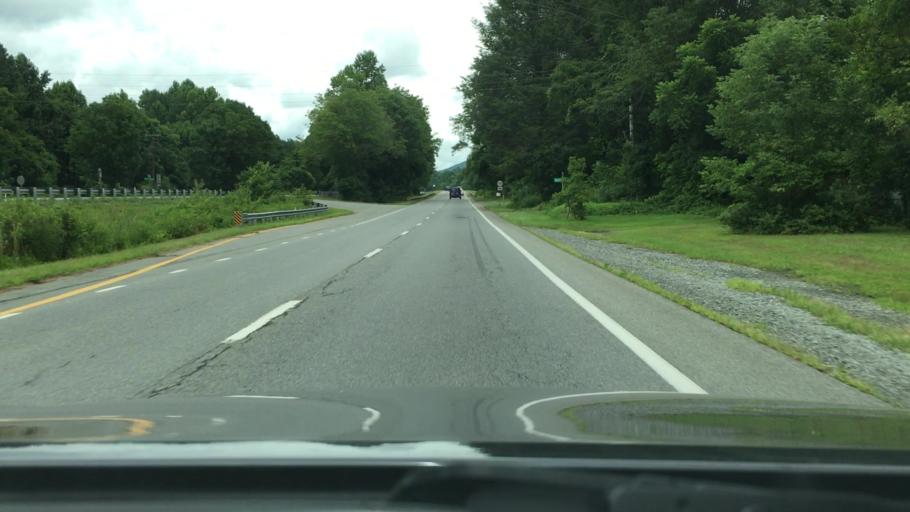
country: US
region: Virginia
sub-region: Nelson County
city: Nellysford
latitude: 37.8947
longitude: -78.6990
